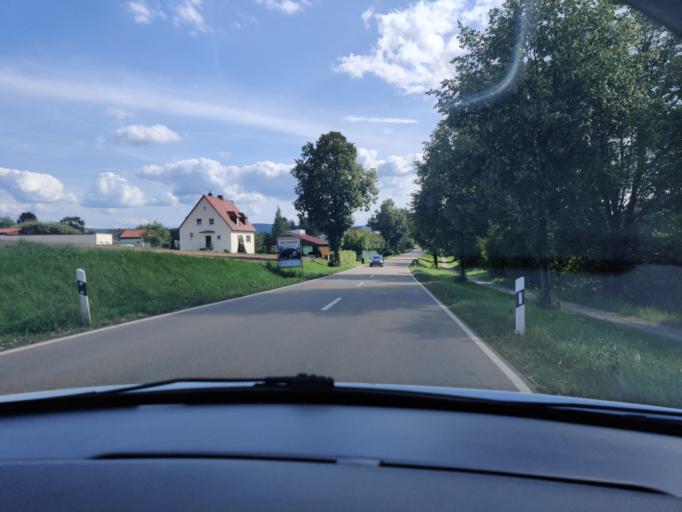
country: DE
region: Bavaria
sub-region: Upper Palatinate
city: Nabburg
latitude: 49.4649
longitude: 12.1865
